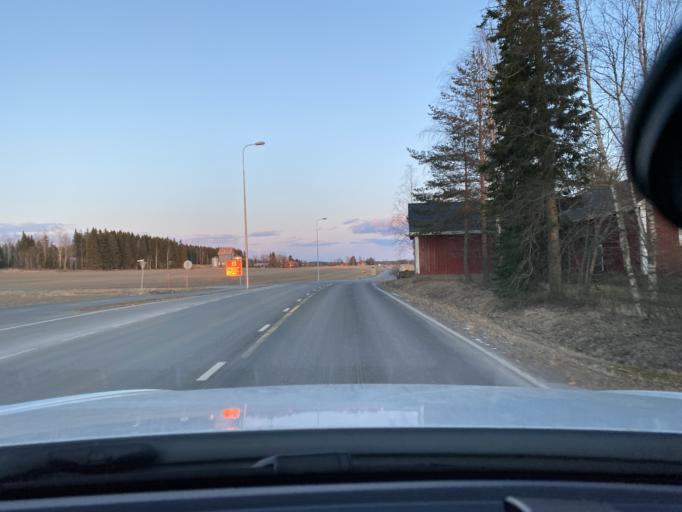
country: FI
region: Pirkanmaa
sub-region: Lounais-Pirkanmaa
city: Punkalaidun
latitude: 61.1073
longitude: 23.1336
